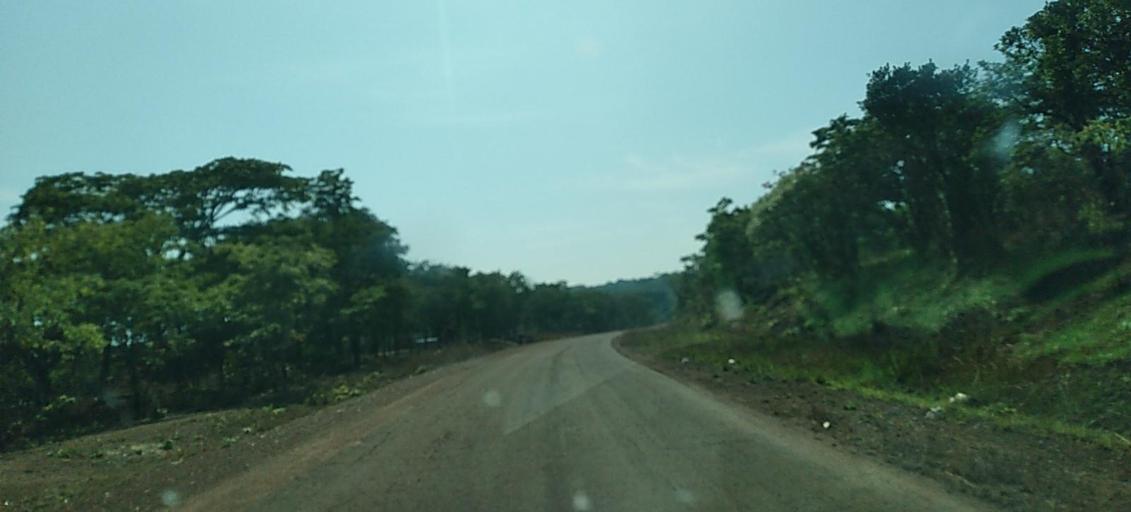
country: ZM
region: North-Western
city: Mwinilunga
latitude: -11.7848
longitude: 25.0423
